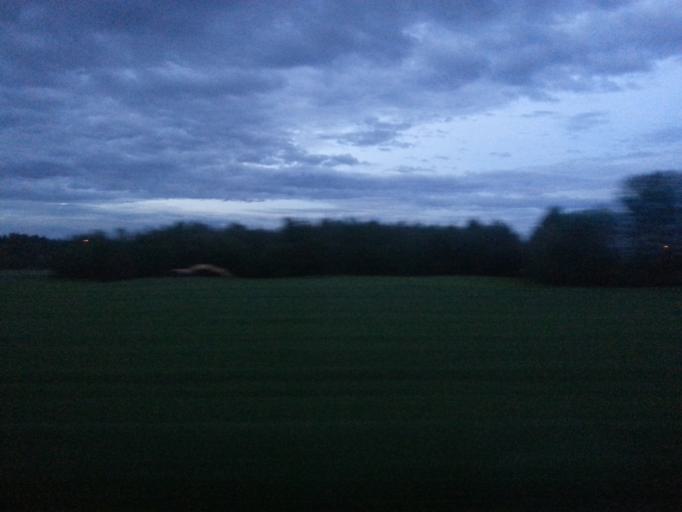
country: NO
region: Akershus
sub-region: Ullensaker
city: Klofta
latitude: 60.0924
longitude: 11.1411
